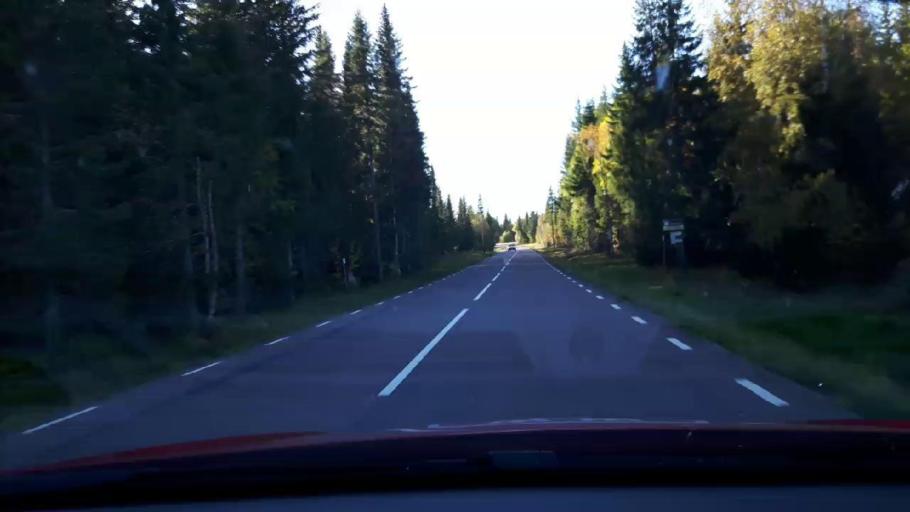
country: SE
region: Jaemtland
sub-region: Stroemsunds Kommun
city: Stroemsund
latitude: 63.8648
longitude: 15.1457
